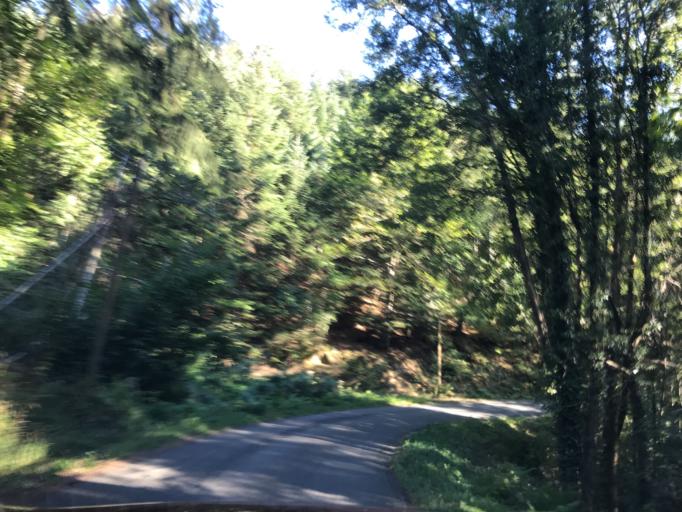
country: FR
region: Auvergne
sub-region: Departement du Puy-de-Dome
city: Escoutoux
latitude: 45.7820
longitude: 3.6078
